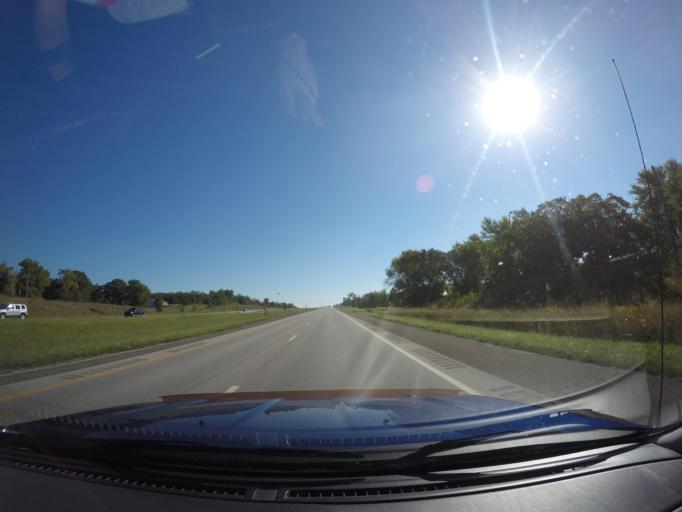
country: US
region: Kansas
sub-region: Riley County
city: Manhattan
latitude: 39.1995
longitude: -96.4463
